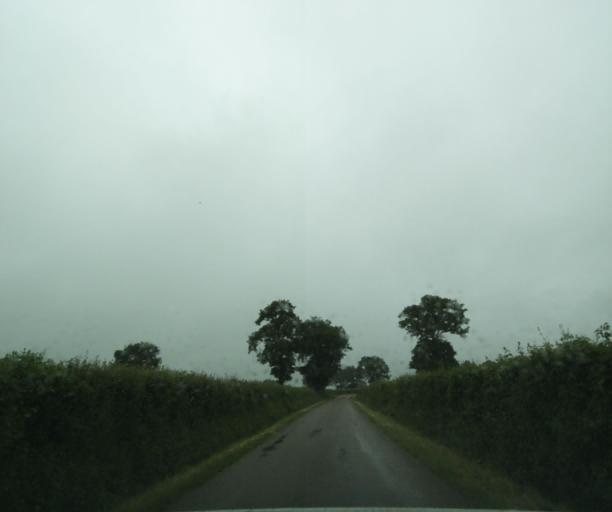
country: FR
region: Bourgogne
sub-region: Departement de Saone-et-Loire
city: Charolles
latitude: 46.4242
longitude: 4.3227
